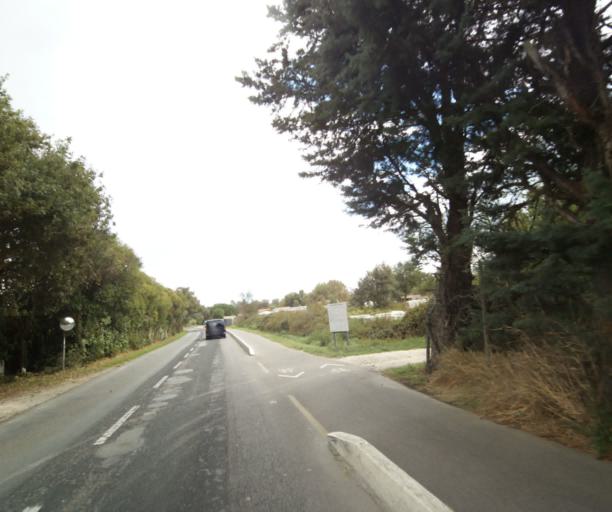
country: FR
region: Languedoc-Roussillon
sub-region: Departement des Pyrenees-Orientales
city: Argelers
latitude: 42.5548
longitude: 3.0274
